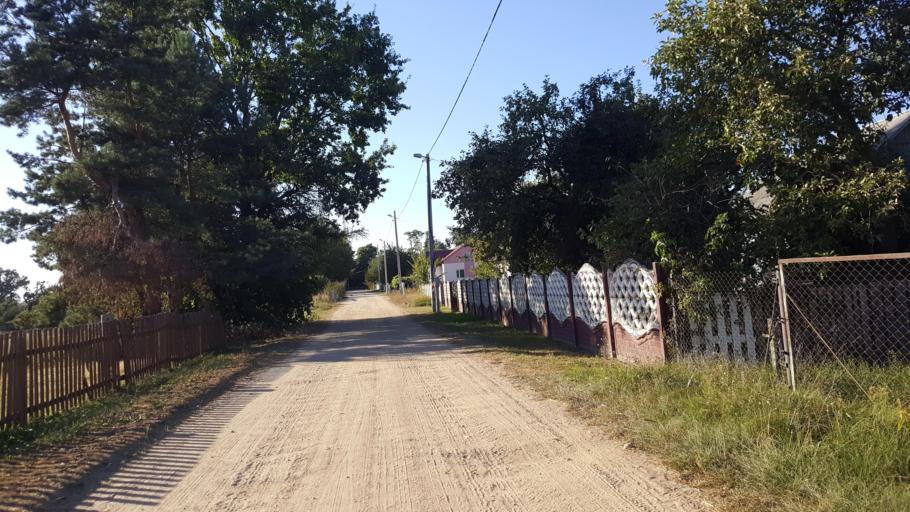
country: BY
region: Brest
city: Vysokaye
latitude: 52.3266
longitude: 23.2721
